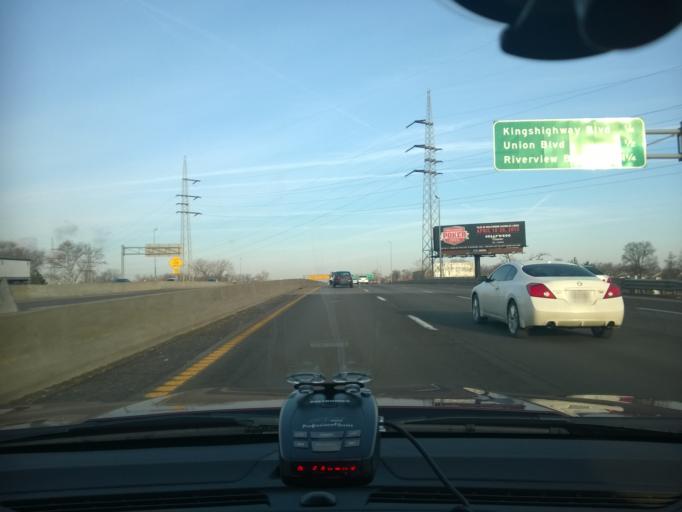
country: US
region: Missouri
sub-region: Saint Louis County
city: Pine Lawn
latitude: 38.6841
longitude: -90.2411
